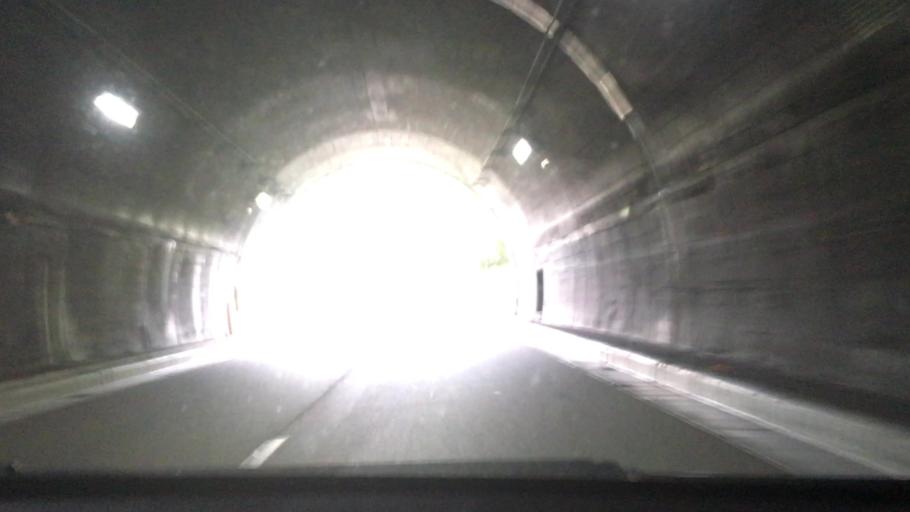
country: JP
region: Yamaguchi
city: Shimonoseki
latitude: 33.9528
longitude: 130.9828
